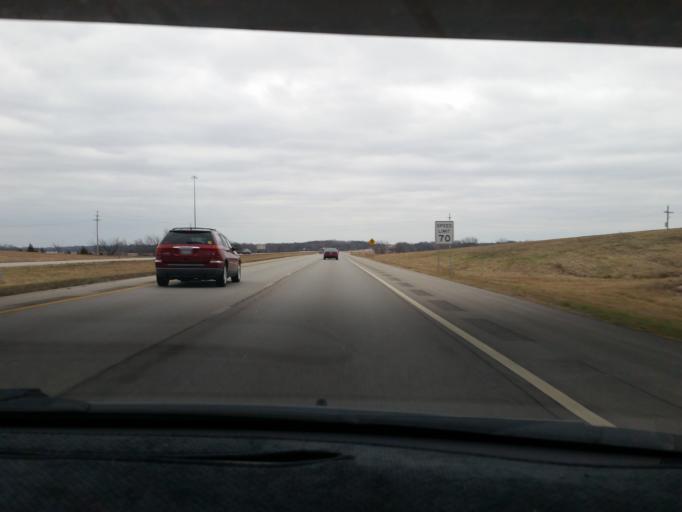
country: US
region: Kansas
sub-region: Douglas County
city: Eudora
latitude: 38.9350
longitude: -95.1493
